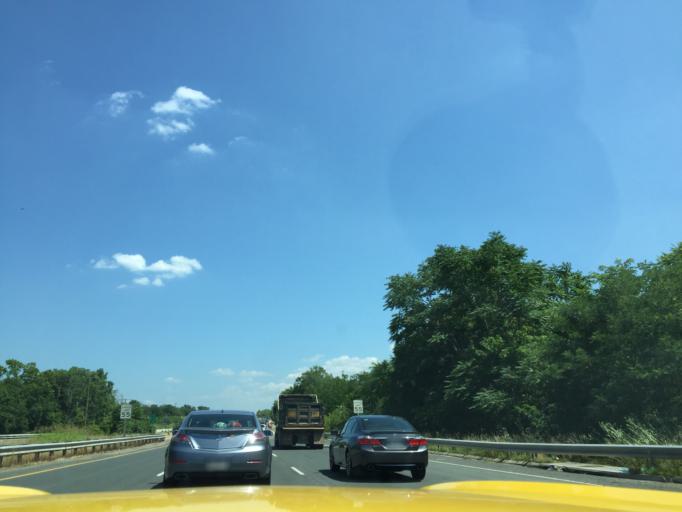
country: US
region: Virginia
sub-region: Loudoun County
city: Belmont
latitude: 39.0865
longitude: -77.5125
